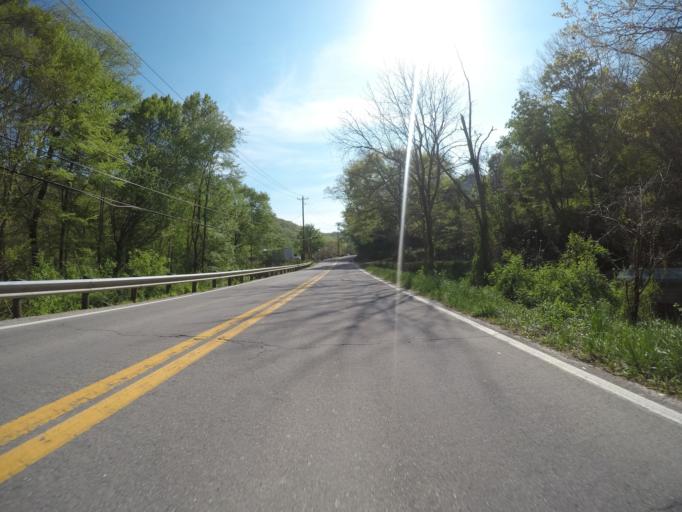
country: US
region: West Virginia
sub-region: Kanawha County
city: Clendenin
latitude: 38.4641
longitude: -81.4058
